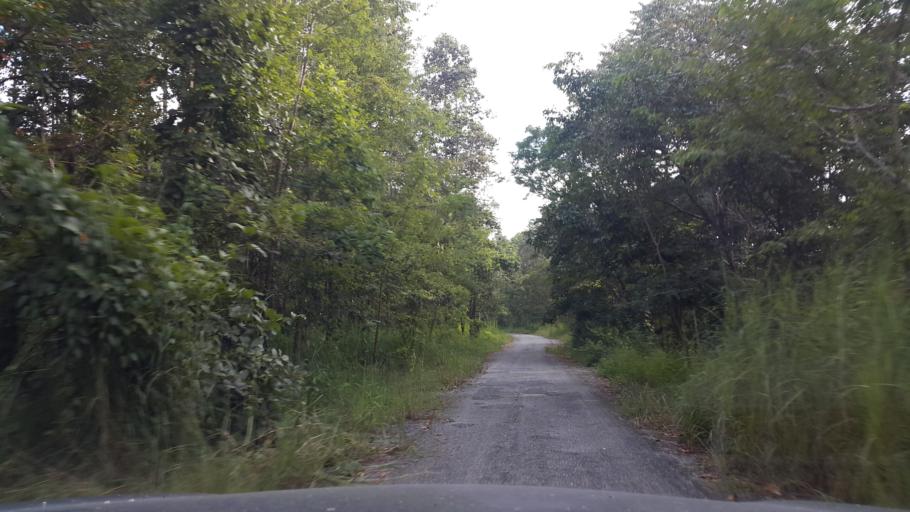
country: TH
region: Chiang Mai
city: San Sai
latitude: 18.9247
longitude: 99.0843
